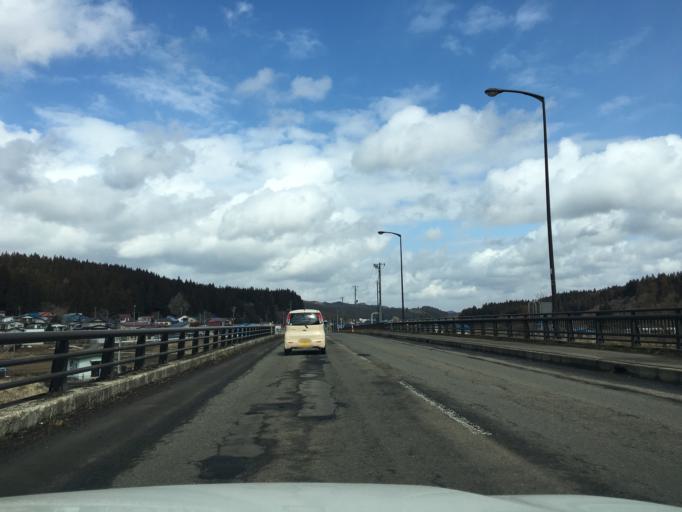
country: JP
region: Akita
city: Takanosu
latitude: 40.0297
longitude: 140.2742
